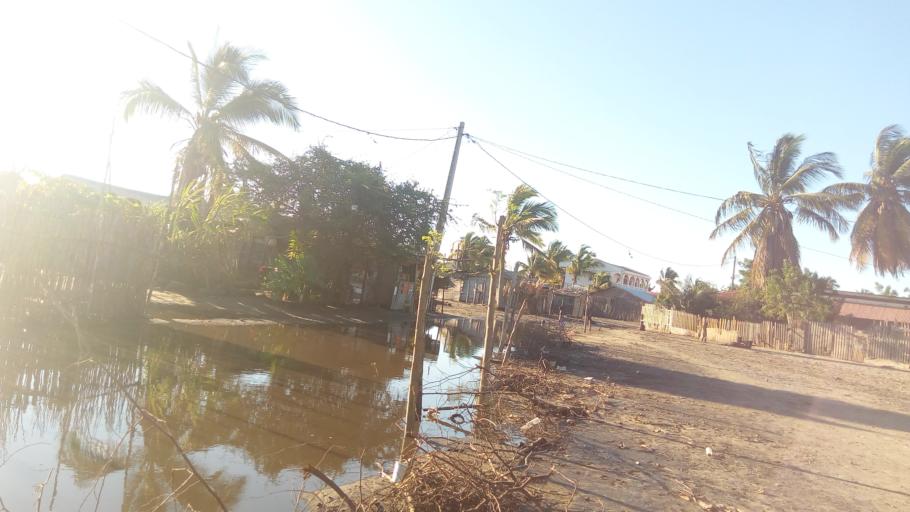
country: MG
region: Menabe
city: Morondava
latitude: -20.2974
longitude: 44.2780
